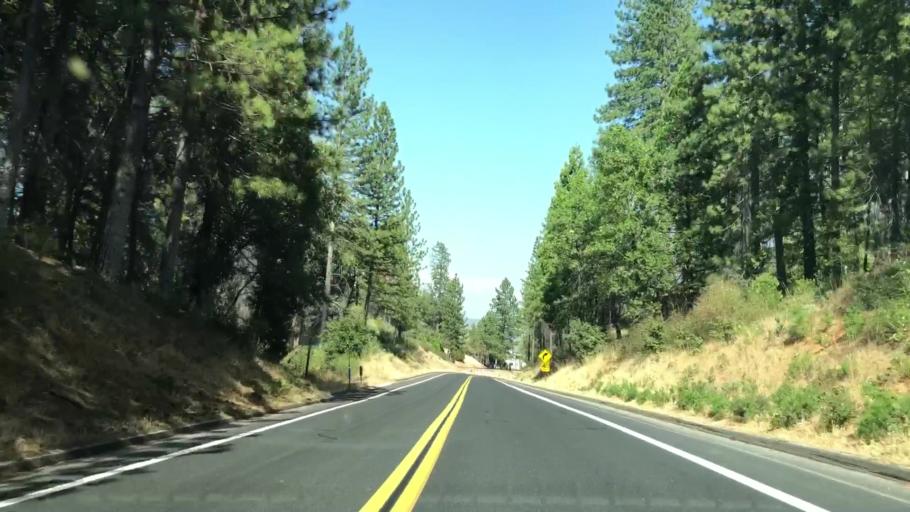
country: US
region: California
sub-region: Tuolumne County
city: Tuolumne City
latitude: 37.8216
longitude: -120.0282
